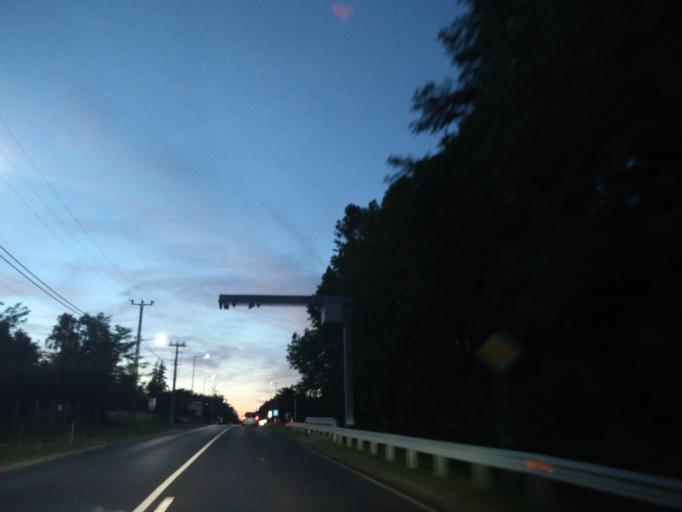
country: HU
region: Zala
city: Zalaegerszeg
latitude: 46.8649
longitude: 16.8538
